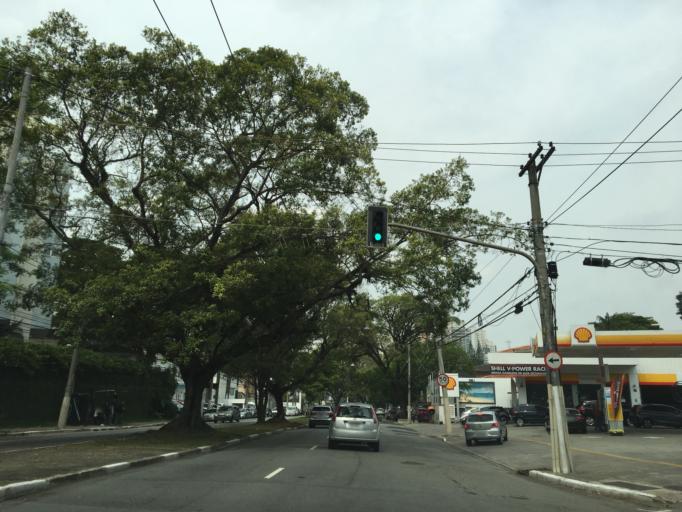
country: BR
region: Sao Paulo
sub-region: Sao Paulo
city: Sao Paulo
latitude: -23.5460
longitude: -46.6691
